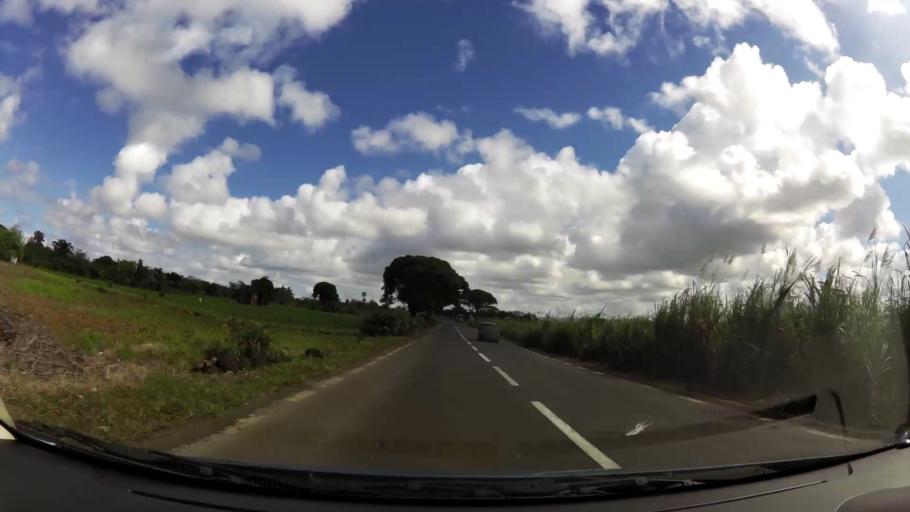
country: MU
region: Grand Port
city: Beau Vallon
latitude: -20.4263
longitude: 57.6878
